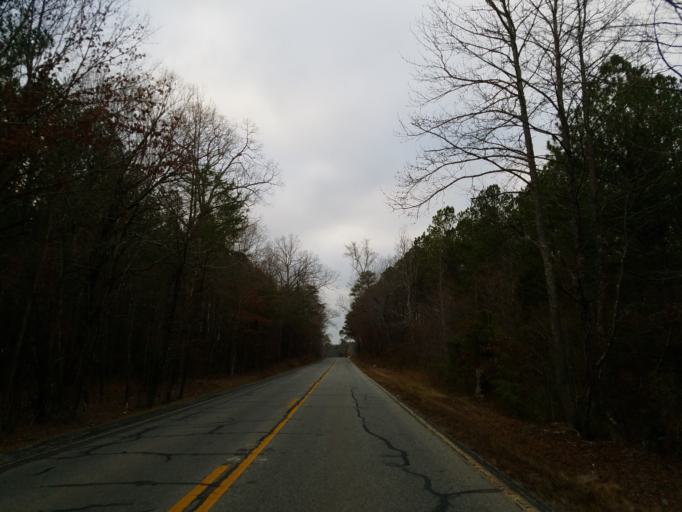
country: US
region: Georgia
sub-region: Bartow County
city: Rydal
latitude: 34.3457
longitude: -84.6919
